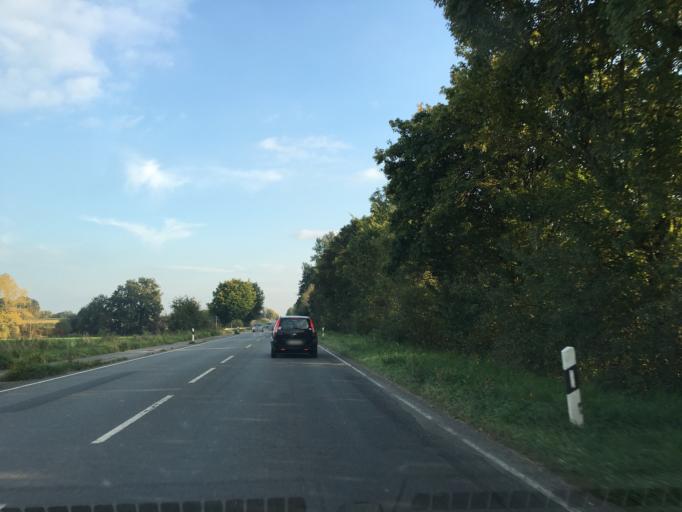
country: DE
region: North Rhine-Westphalia
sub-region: Regierungsbezirk Munster
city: Altenberge
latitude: 52.0361
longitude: 7.4770
